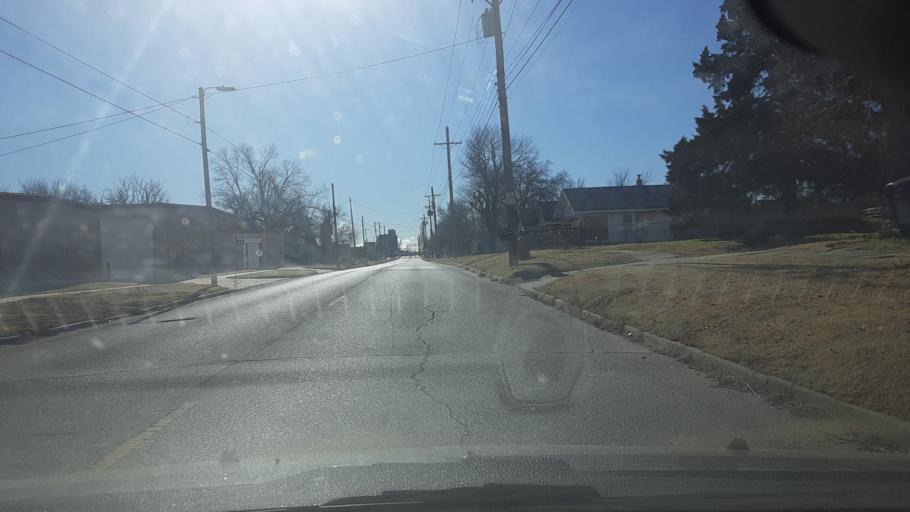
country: US
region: Oklahoma
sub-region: Kay County
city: Ponca City
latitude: 36.7127
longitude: -97.0853
